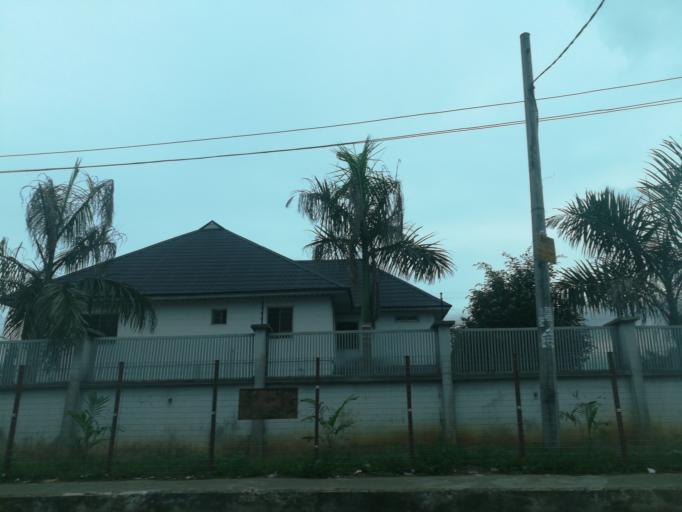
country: NG
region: Rivers
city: Port Harcourt
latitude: 4.8205
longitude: 6.9952
